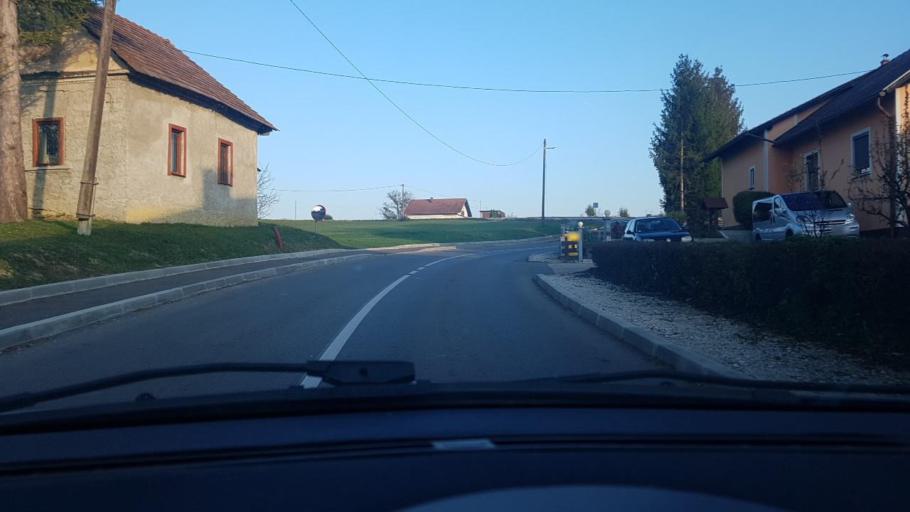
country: SI
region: Rogaska Slatina
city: Rogaska Slatina
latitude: 46.2142
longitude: 15.6578
